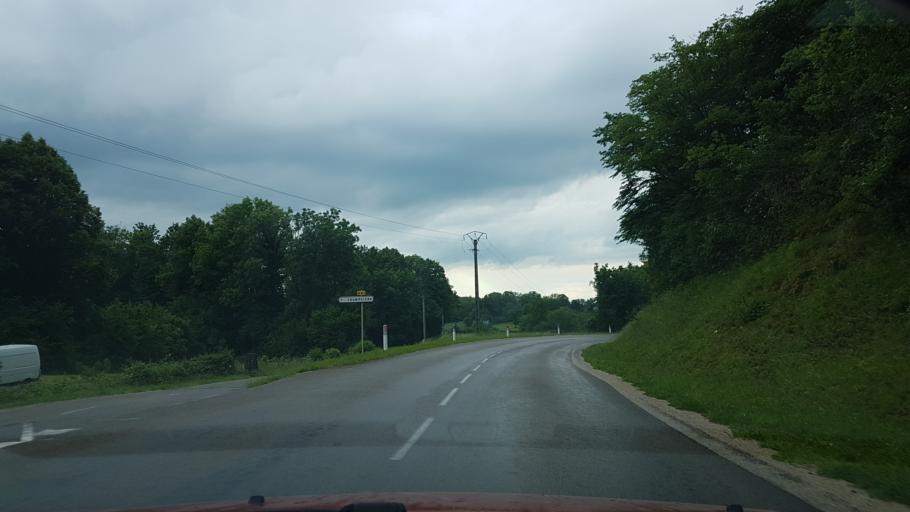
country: FR
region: Franche-Comte
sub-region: Departement du Jura
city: Clairvaux-les-Lacs
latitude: 46.5498
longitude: 5.7451
